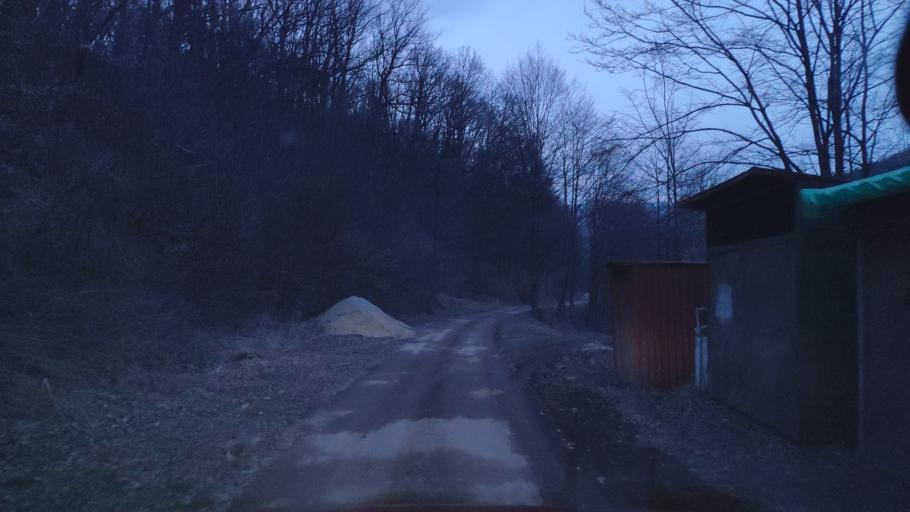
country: SK
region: Kosicky
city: Medzev
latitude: 48.7168
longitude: 20.9246
